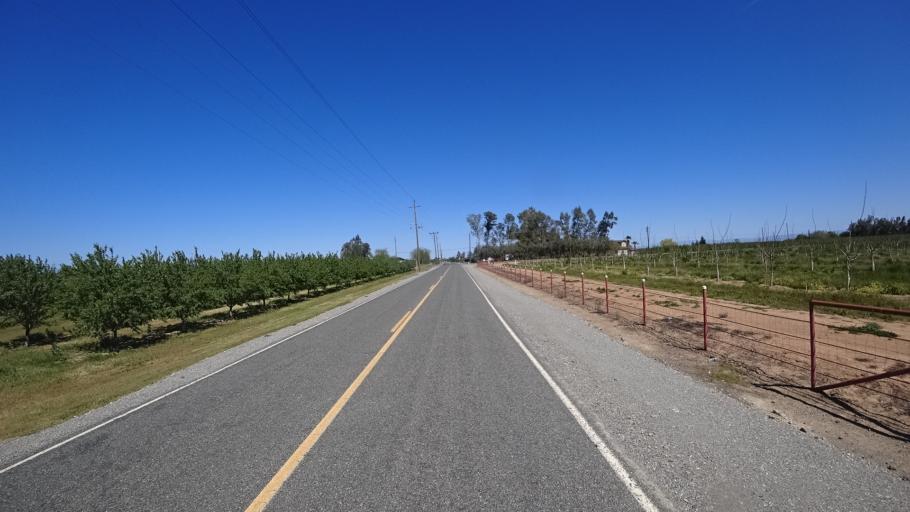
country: US
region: California
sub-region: Glenn County
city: Orland
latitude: 39.6954
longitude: -122.1779
